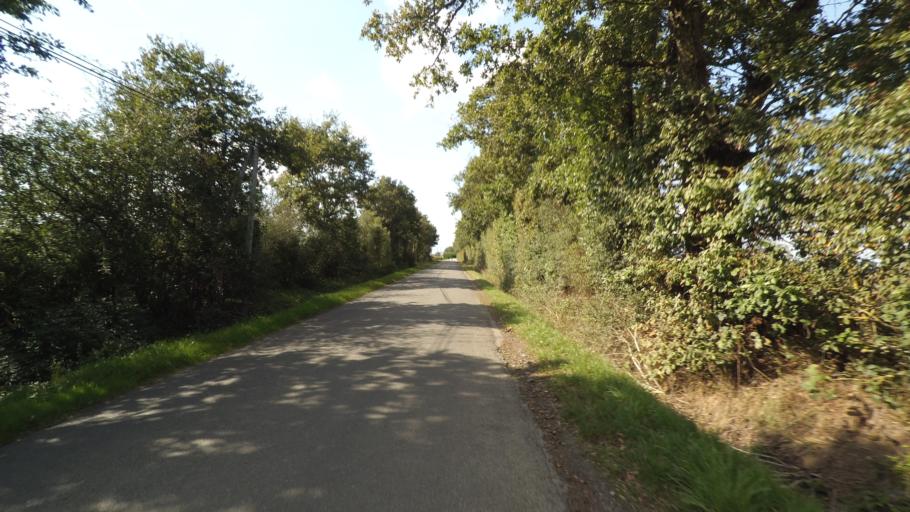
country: FR
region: Pays de la Loire
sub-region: Departement de la Vendee
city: Saint-Andre-Treize-Voies
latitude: 46.9630
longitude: -1.3839
